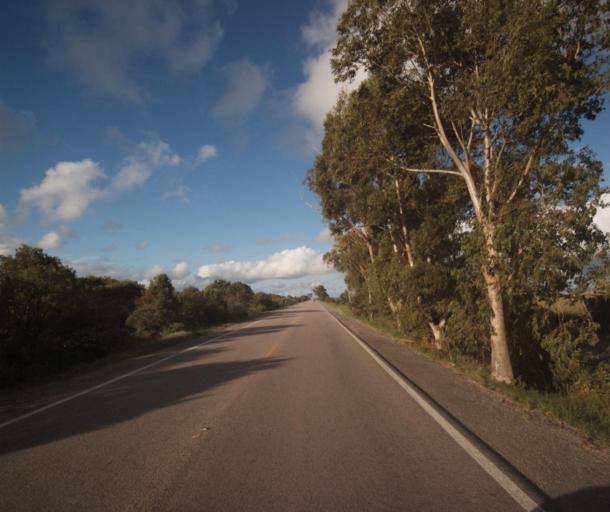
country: BR
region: Rio Grande do Sul
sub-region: Rio Grande
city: Rio Grande
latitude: -32.1807
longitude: -52.4231
